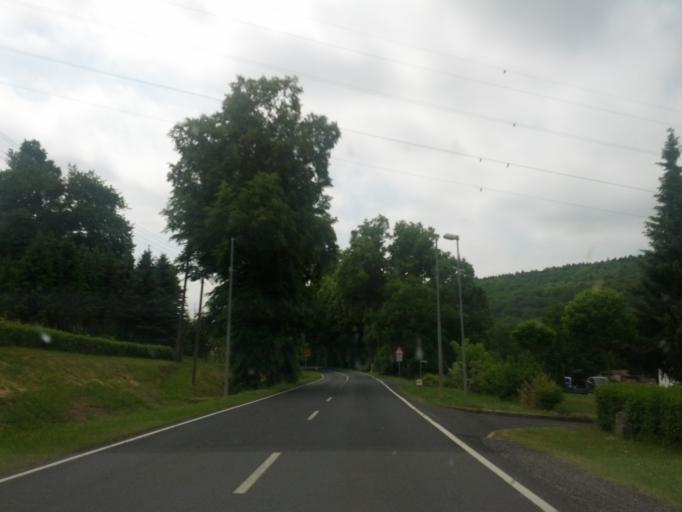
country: DE
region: Thuringia
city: Martinroda
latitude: 50.8118
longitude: 10.0899
